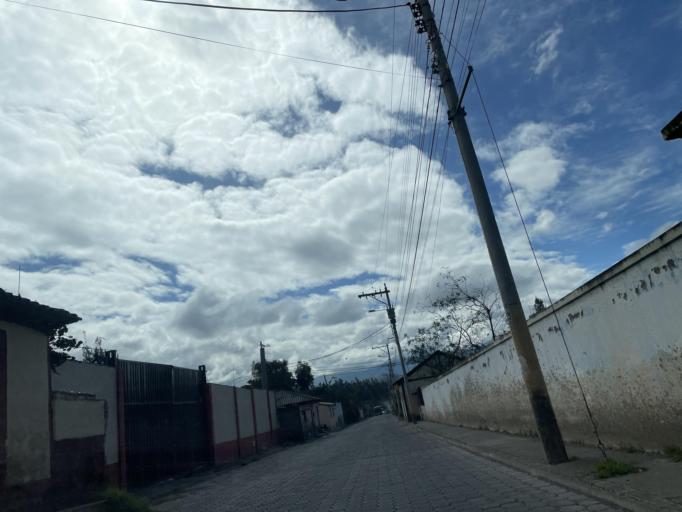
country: EC
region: Chimborazo
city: Guano
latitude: -1.6071
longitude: -78.6276
